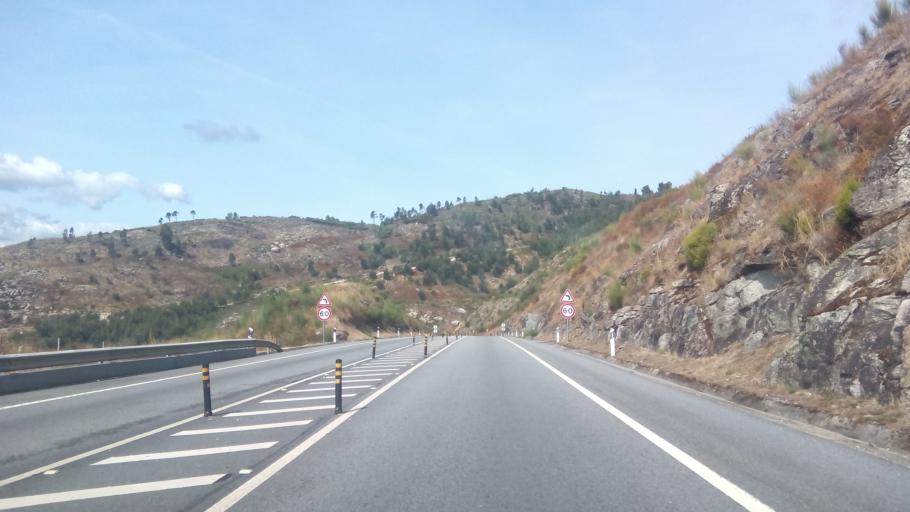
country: PT
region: Porto
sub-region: Amarante
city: Amarante
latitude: 41.2653
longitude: -7.9793
